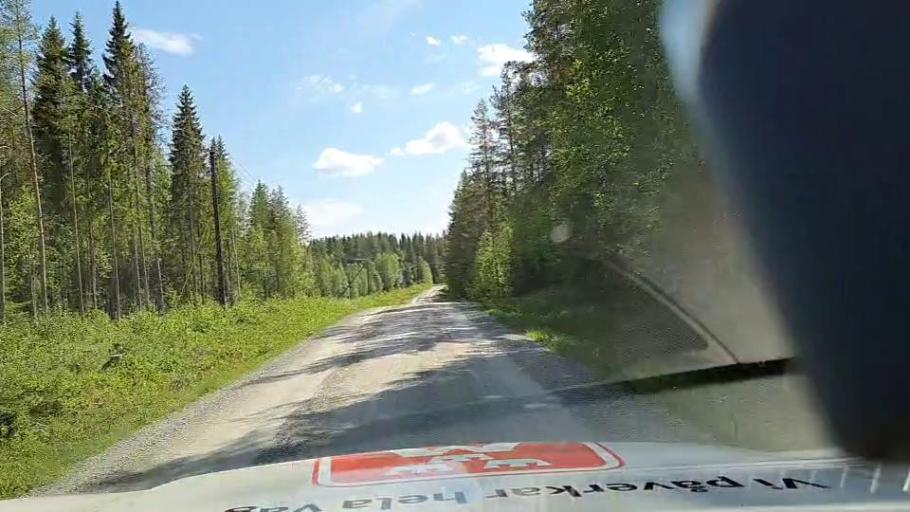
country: SE
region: Jaemtland
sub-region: Stroemsunds Kommun
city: Stroemsund
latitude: 64.4684
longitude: 15.5946
